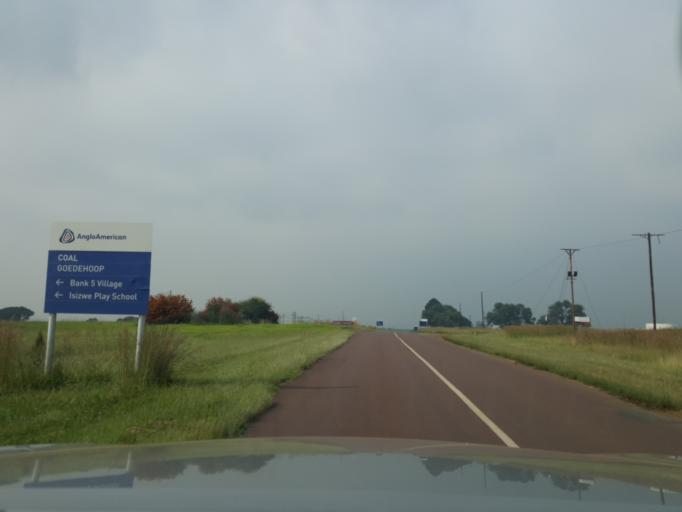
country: ZA
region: Mpumalanga
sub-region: Nkangala District Municipality
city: Middelburg
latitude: -26.0015
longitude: 29.4506
